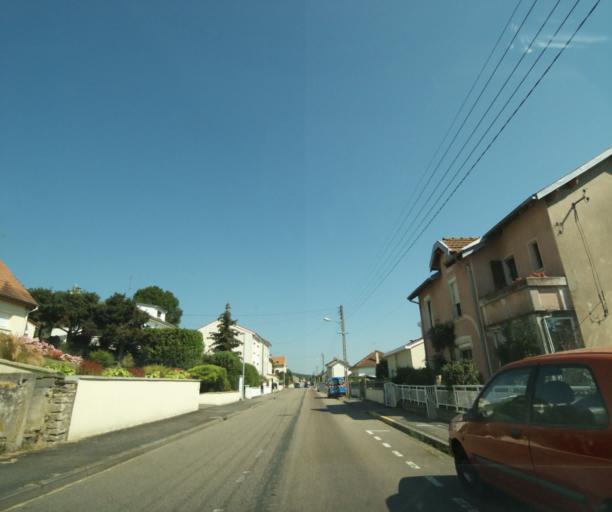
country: FR
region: Lorraine
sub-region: Departement de Meurthe-et-Moselle
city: Toul
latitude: 48.6646
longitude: 5.8848
